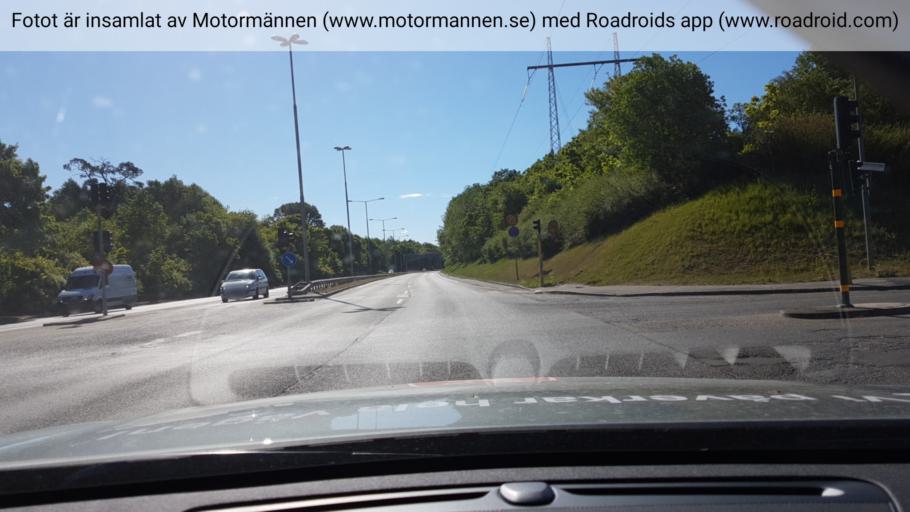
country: SE
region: Stockholm
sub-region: Stockholms Kommun
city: Arsta
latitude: 59.2739
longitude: 18.0445
